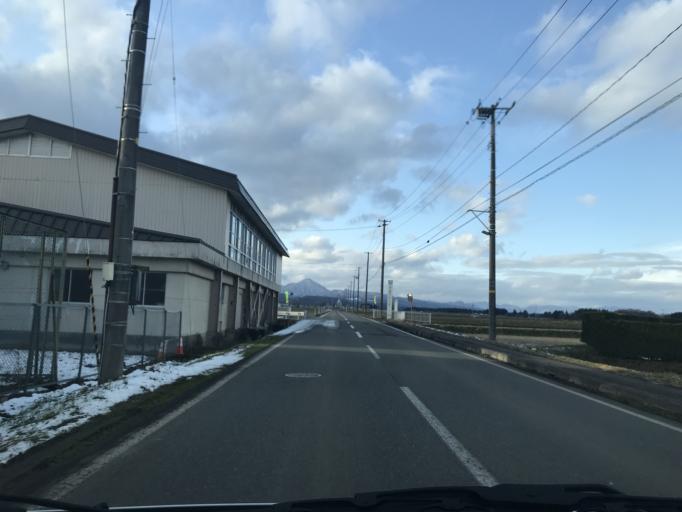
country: JP
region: Iwate
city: Mizusawa
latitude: 39.1975
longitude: 141.0676
